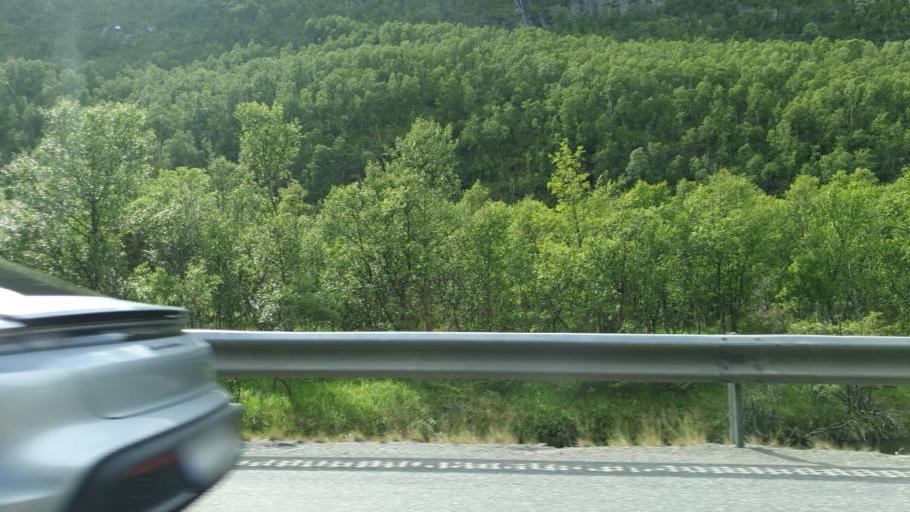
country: NO
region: Sor-Trondelag
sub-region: Oppdal
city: Oppdal
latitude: 62.3668
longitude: 9.6364
